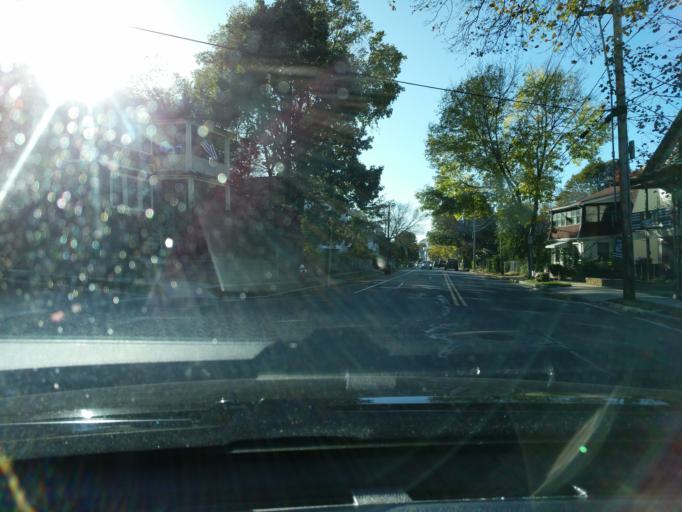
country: US
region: Massachusetts
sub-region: Middlesex County
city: Watertown
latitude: 42.3803
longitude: -71.1818
